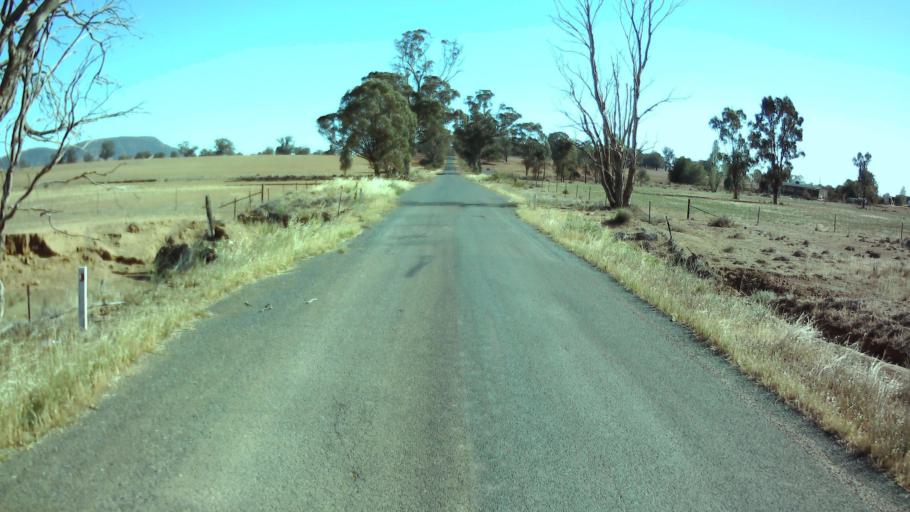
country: AU
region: New South Wales
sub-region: Weddin
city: Grenfell
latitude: -33.7933
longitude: 147.9571
